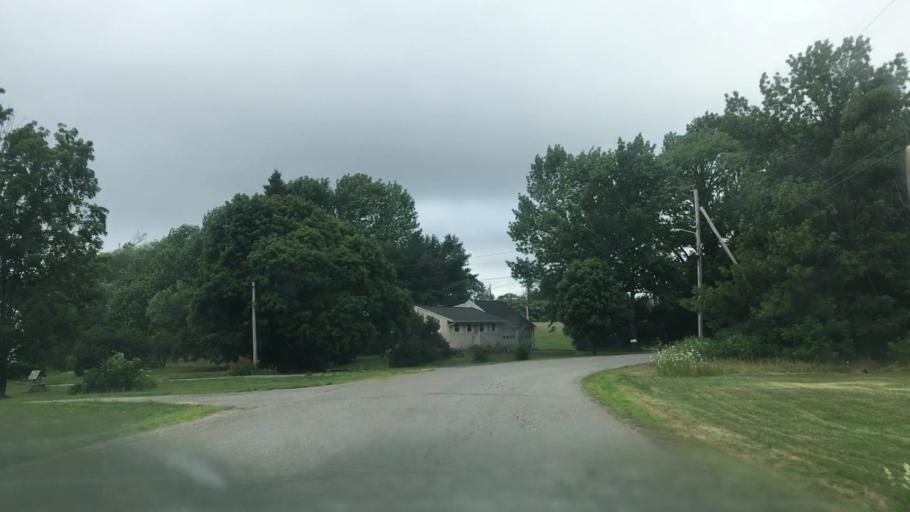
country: US
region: Maine
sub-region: Penobscot County
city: Veazie
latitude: 44.8468
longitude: -68.7468
